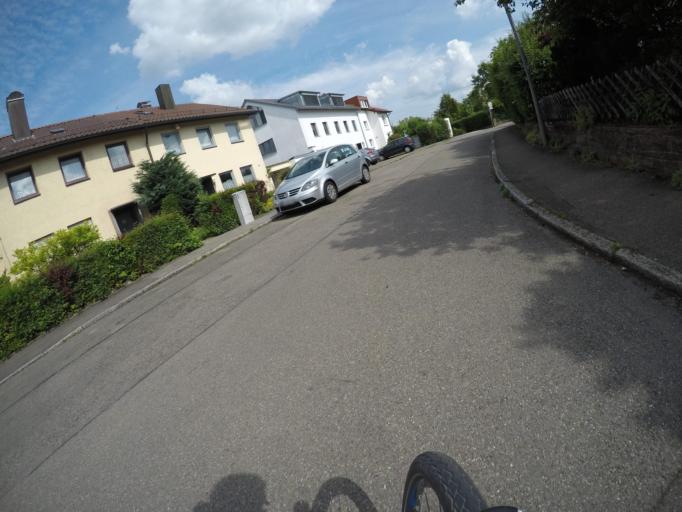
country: DE
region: Baden-Wuerttemberg
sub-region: Regierungsbezirk Stuttgart
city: Boeblingen
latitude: 48.6783
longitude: 9.0019
